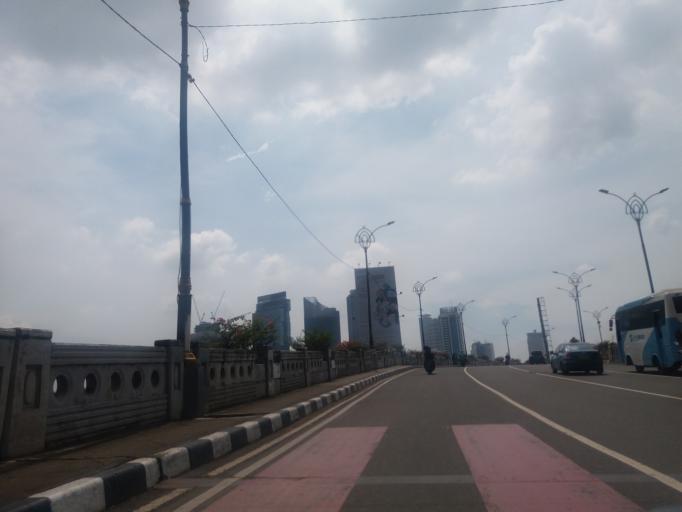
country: ID
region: Jakarta Raya
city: Jakarta
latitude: -6.2051
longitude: 106.8281
